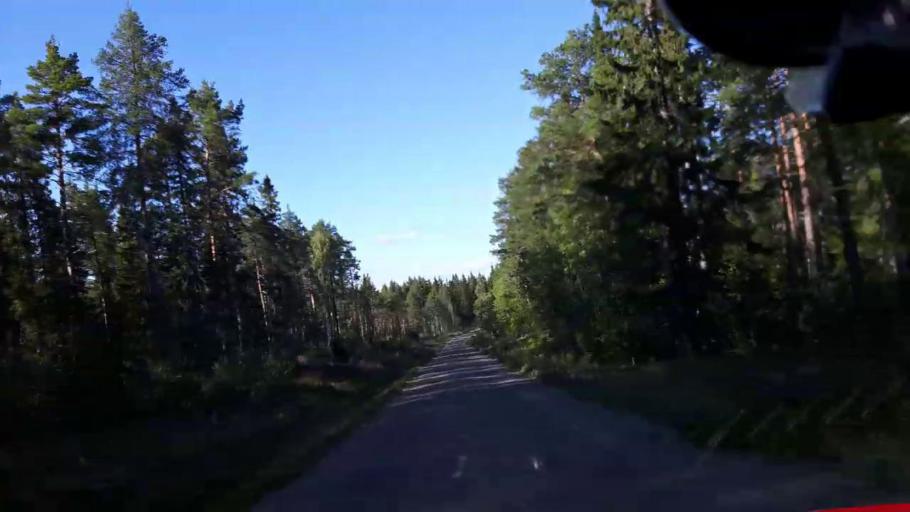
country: SE
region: Jaemtland
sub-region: Ragunda Kommun
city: Hammarstrand
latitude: 63.5217
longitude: 16.0561
